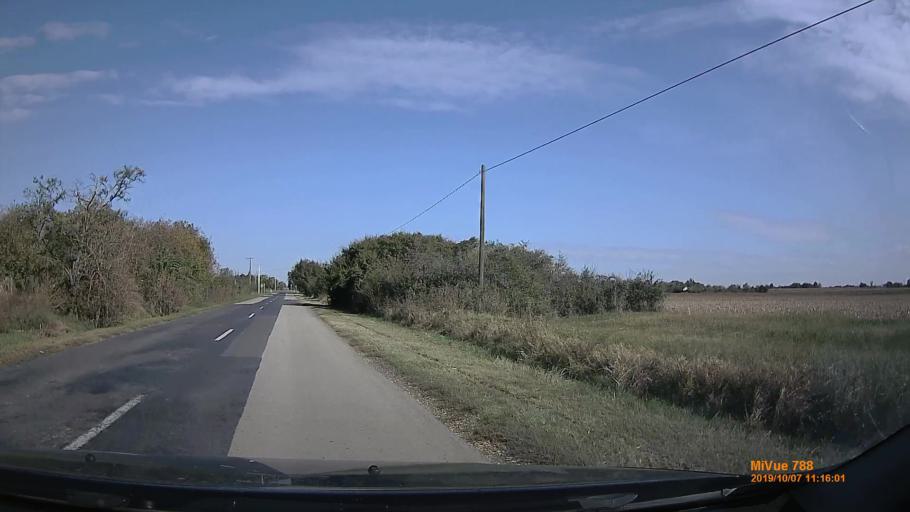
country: HU
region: Bekes
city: Kondoros
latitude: 46.7313
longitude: 20.7810
